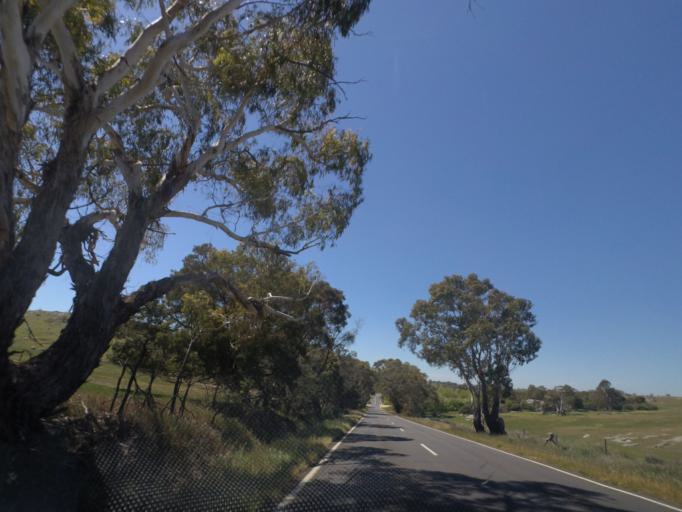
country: AU
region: Victoria
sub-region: Hume
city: Sunbury
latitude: -37.1756
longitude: 144.7483
